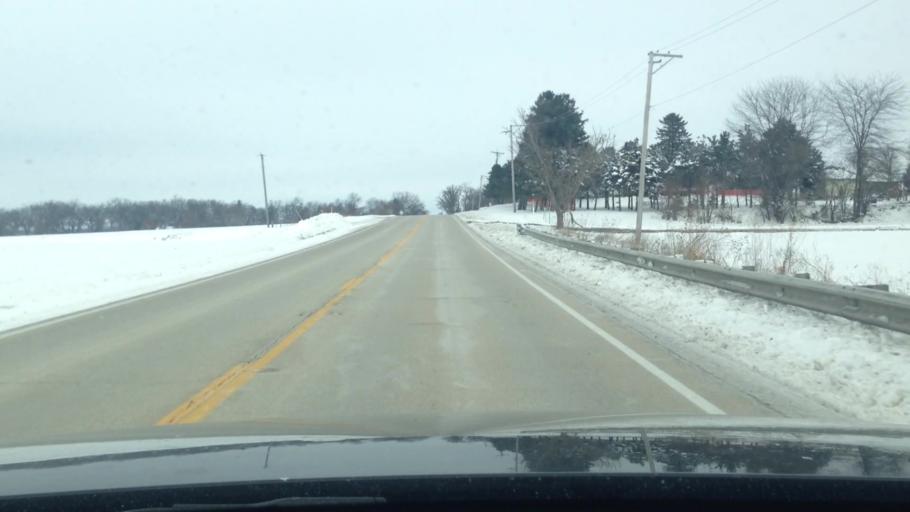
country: US
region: Illinois
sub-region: McHenry County
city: Hebron
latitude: 42.4023
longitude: -88.4382
